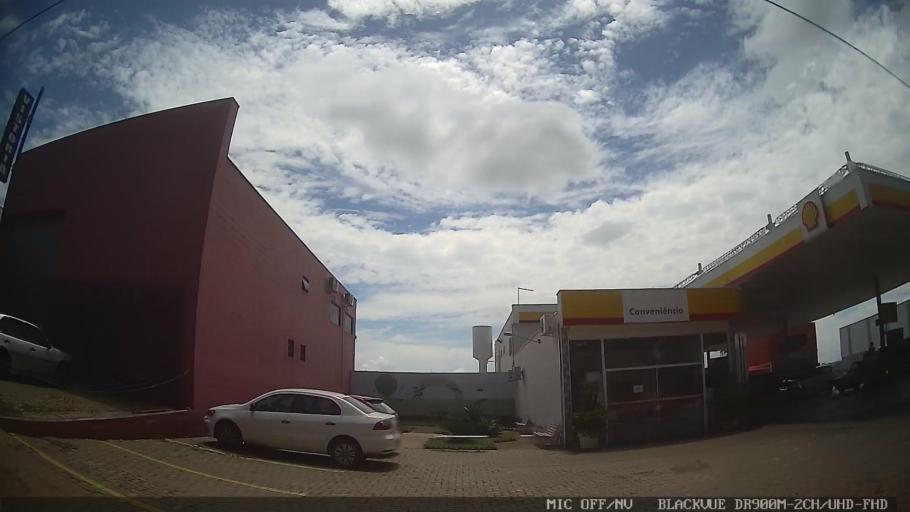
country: BR
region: Sao Paulo
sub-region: Laranjal Paulista
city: Laranjal Paulista
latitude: -23.0601
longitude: -47.8311
